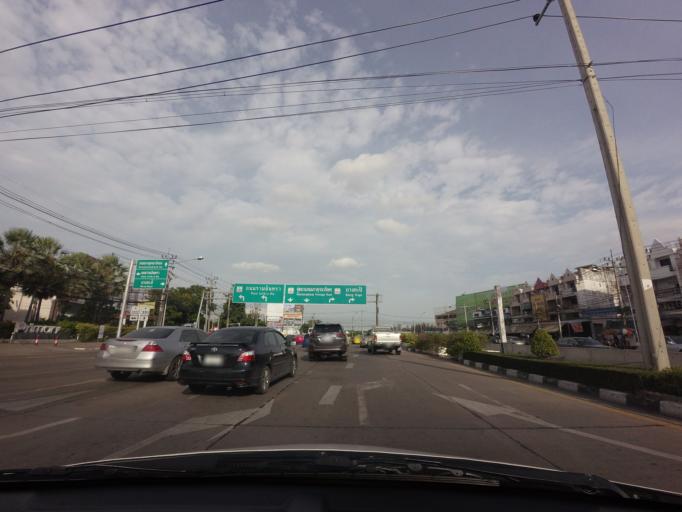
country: TH
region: Bangkok
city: Bueng Kum
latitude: 13.8106
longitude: 100.6492
